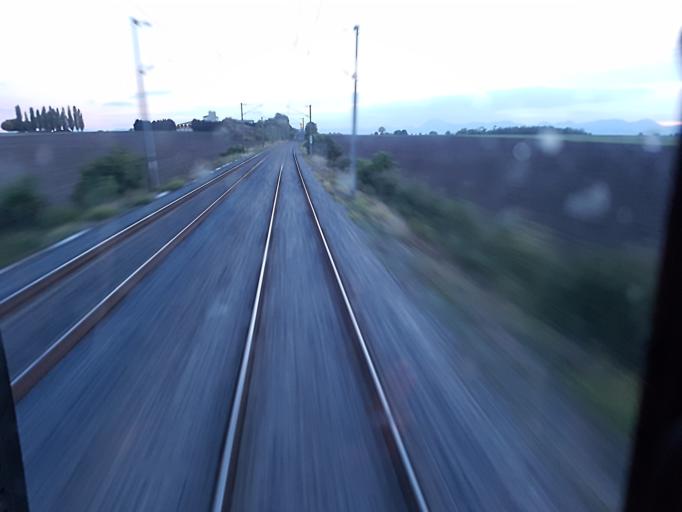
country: FR
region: Auvergne
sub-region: Departement du Puy-de-Dome
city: Ennezat
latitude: 45.9250
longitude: 3.2278
